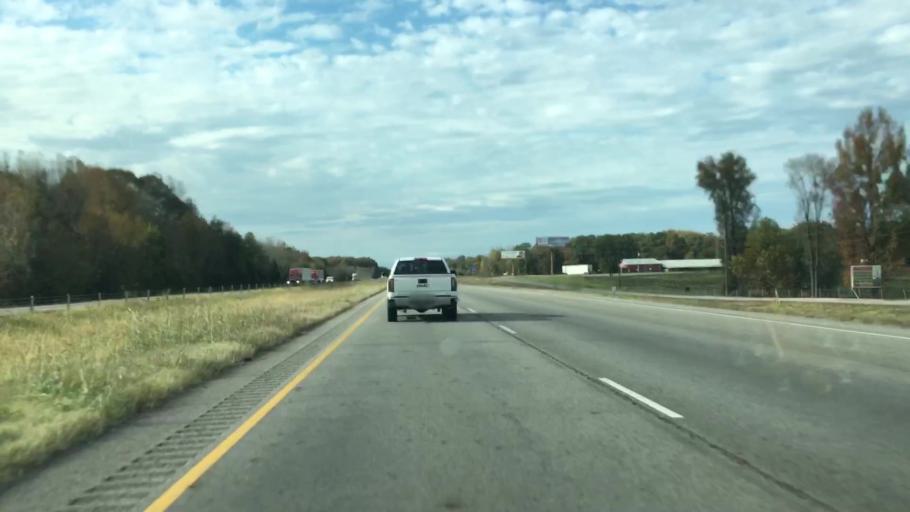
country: US
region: Arkansas
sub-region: Pope County
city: Atkins
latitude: 35.2228
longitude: -92.8345
